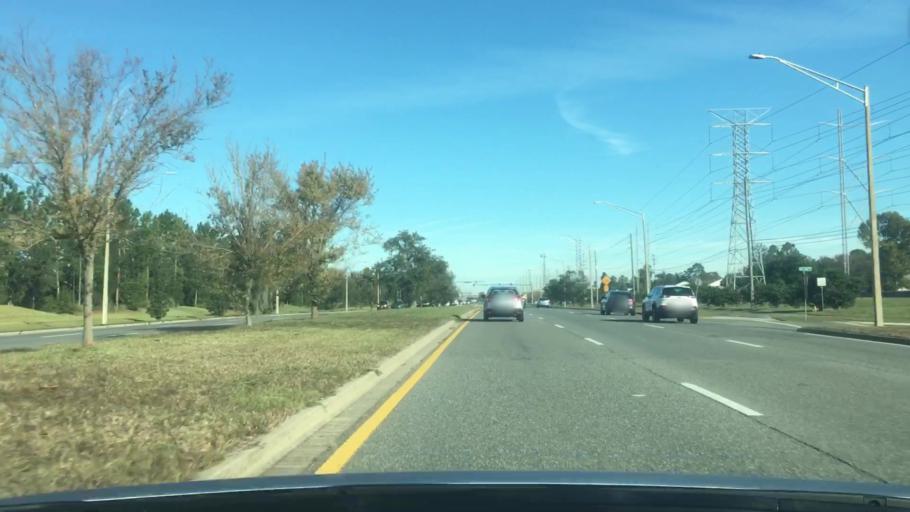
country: US
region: Florida
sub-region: Duval County
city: Neptune Beach
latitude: 30.3096
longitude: -81.4891
